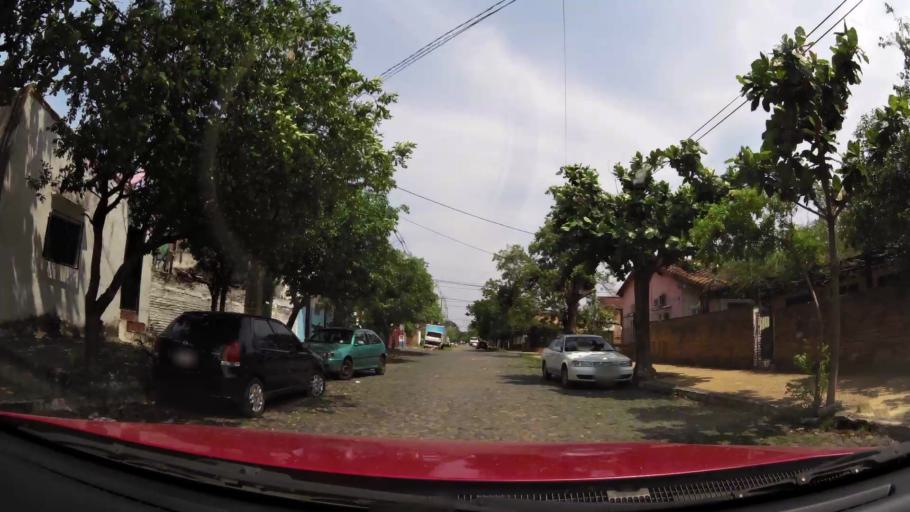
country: PY
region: Asuncion
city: Asuncion
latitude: -25.2735
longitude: -57.6022
